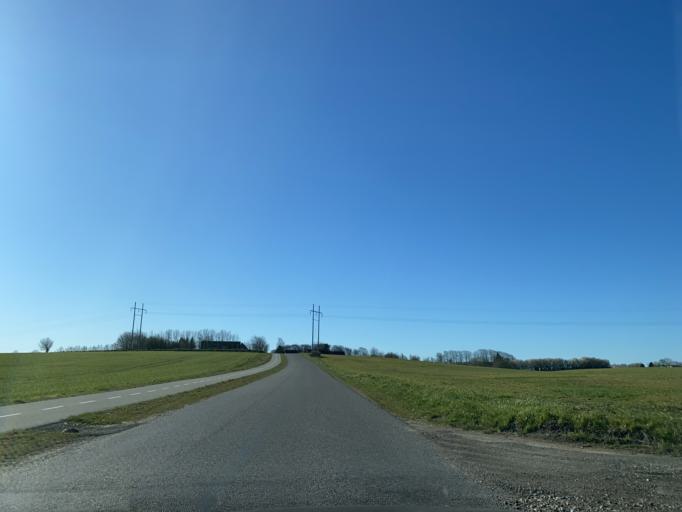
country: DK
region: Central Jutland
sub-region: Skanderborg Kommune
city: Skovby
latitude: 56.1989
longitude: 9.9674
